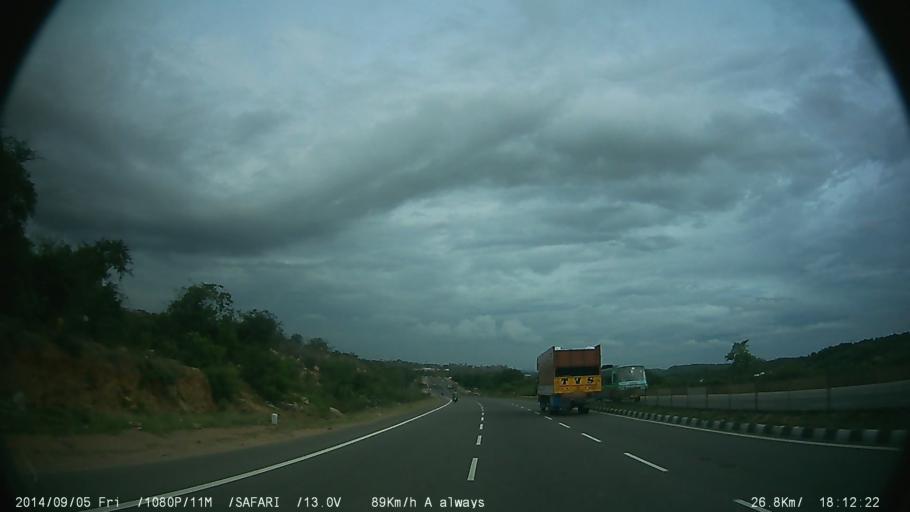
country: IN
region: Tamil Nadu
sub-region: Krishnagiri
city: Hosur
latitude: 12.6928
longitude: 77.9178
